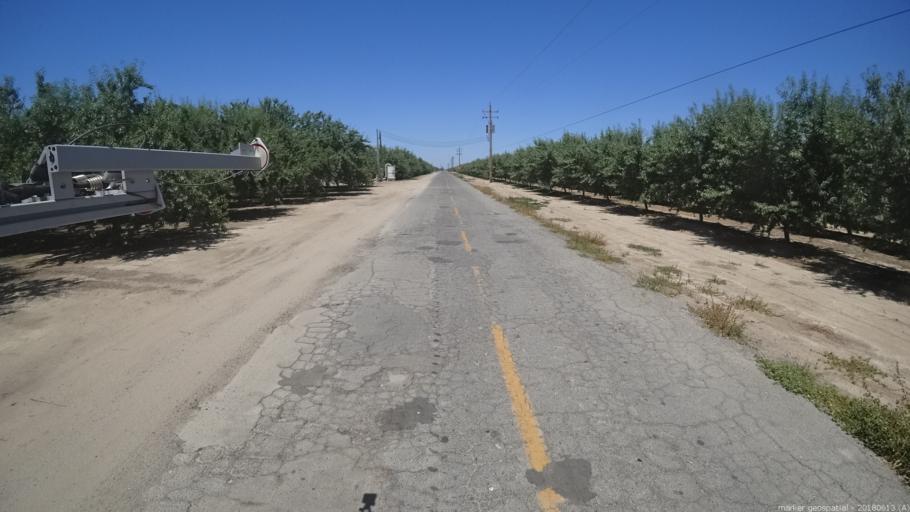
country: US
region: California
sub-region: Madera County
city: Fairmead
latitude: 37.0086
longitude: -120.2743
